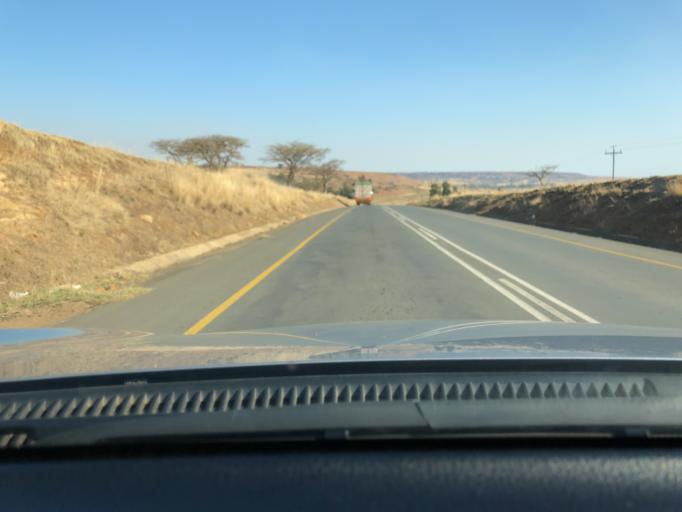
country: ZA
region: KwaZulu-Natal
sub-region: uMzinyathi District Municipality
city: Glencoe
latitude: -28.3188
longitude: 30.0596
